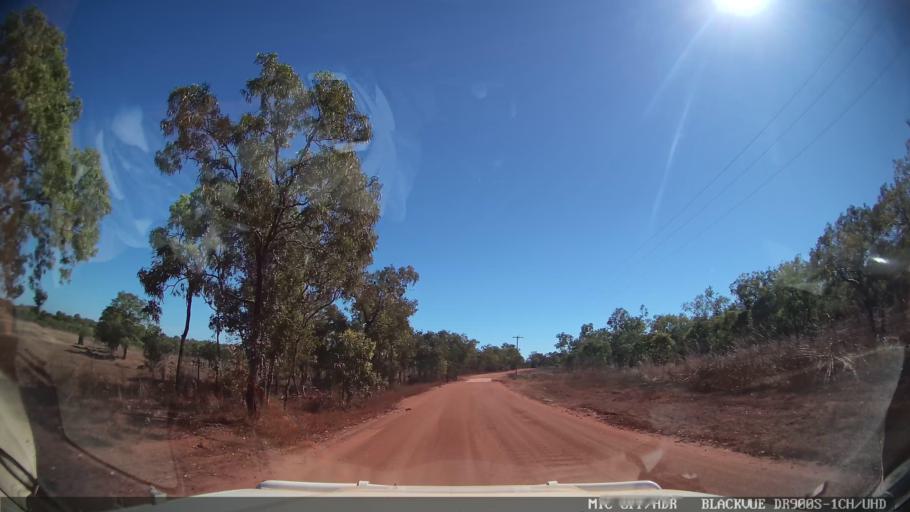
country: AU
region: Queensland
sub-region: Torres
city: Thursday Island
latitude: -10.8533
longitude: 142.3761
